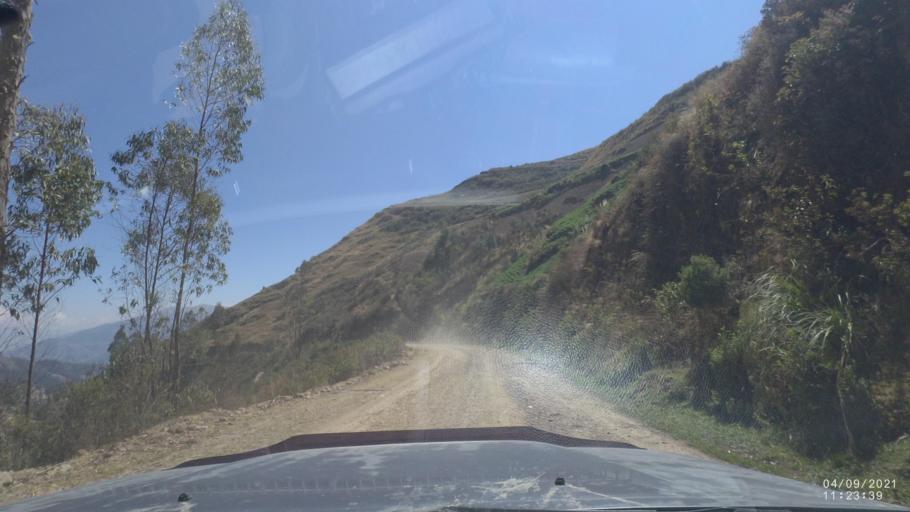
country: BO
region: Cochabamba
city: Colchani
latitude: -17.2624
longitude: -66.5075
